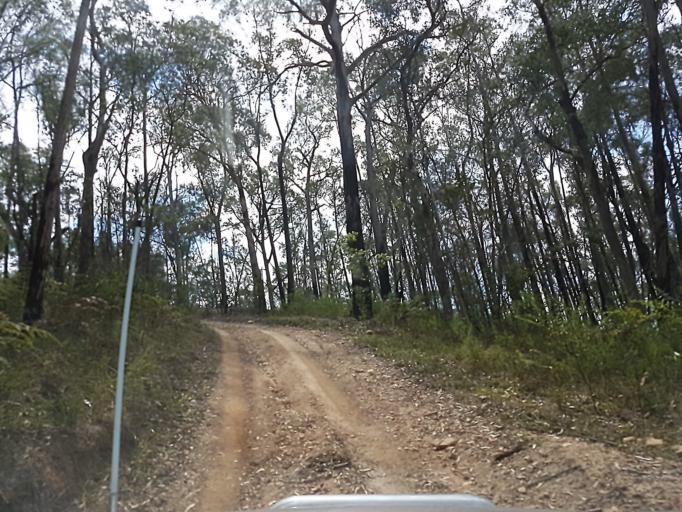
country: AU
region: Victoria
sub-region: East Gippsland
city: Lakes Entrance
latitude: -37.3464
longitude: 148.3572
